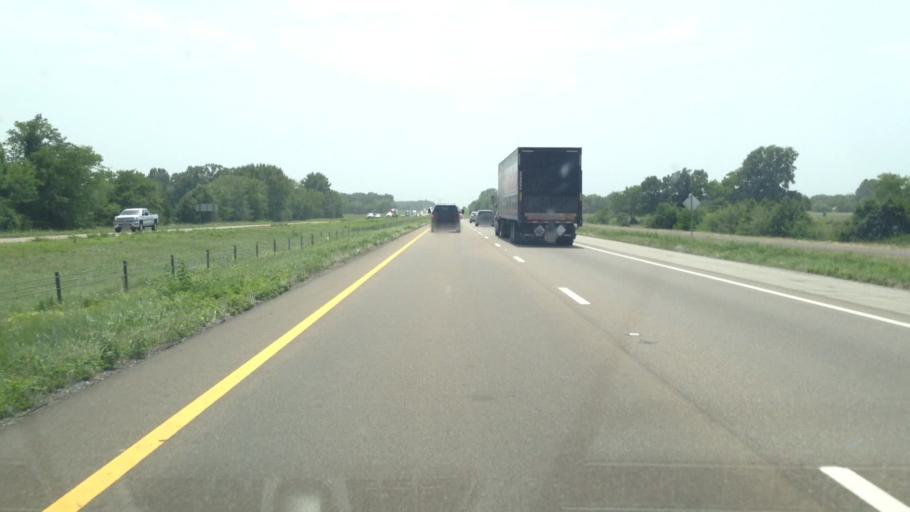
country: US
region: Texas
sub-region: Morris County
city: Omaha
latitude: 33.2523
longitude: -94.8468
